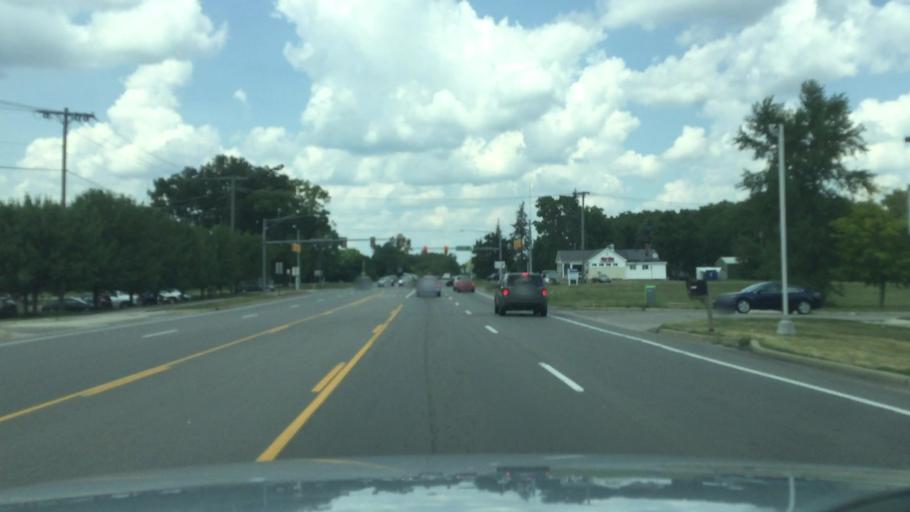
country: US
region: Michigan
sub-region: Washtenaw County
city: Ypsilanti
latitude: 42.2137
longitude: -83.6192
